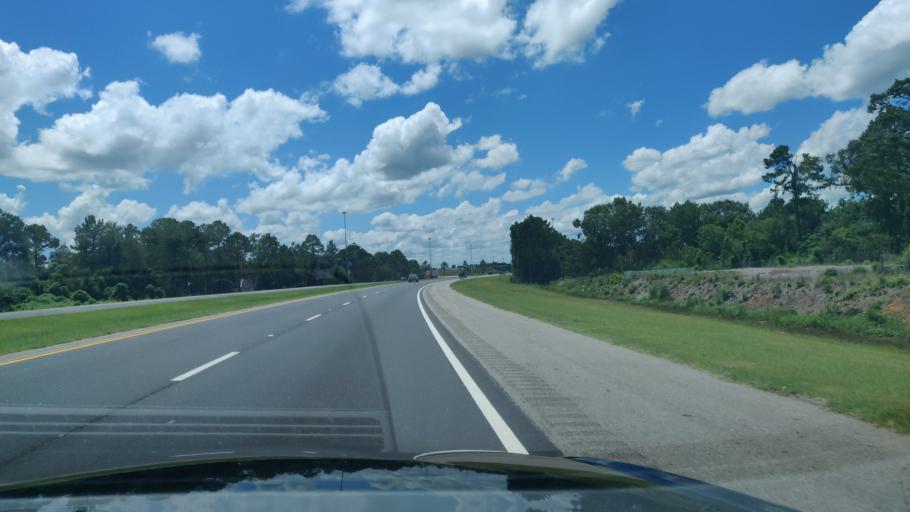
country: US
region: Georgia
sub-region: Dougherty County
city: Albany
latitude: 31.6153
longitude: -84.1953
